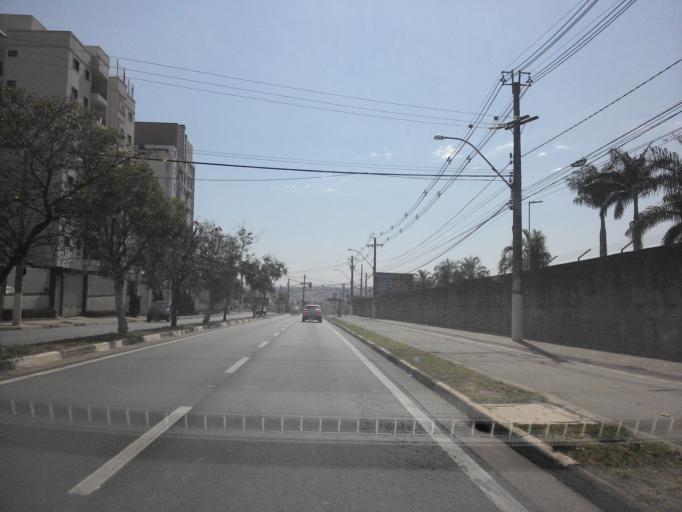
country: BR
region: Sao Paulo
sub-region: Hortolandia
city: Hortolandia
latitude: -22.8763
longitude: -47.2290
